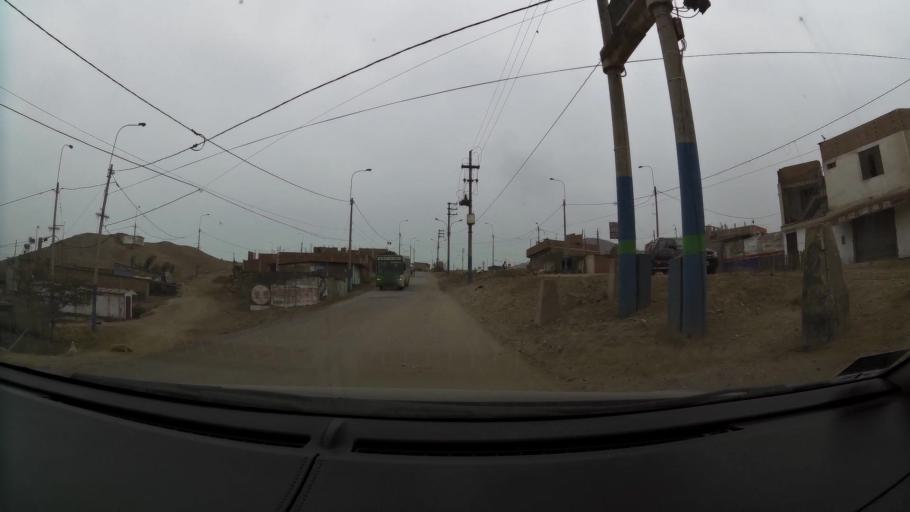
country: PE
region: Lima
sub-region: Lima
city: Santa Rosa
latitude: -11.8347
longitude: -77.1652
